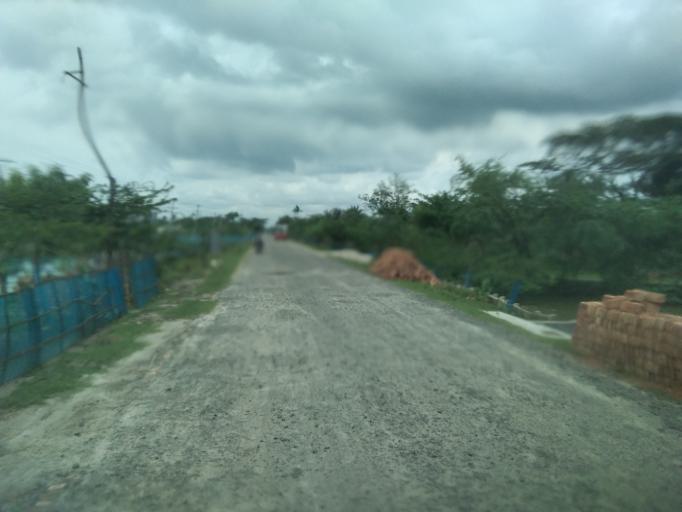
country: IN
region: West Bengal
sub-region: North 24 Parganas
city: Gosaba
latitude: 22.2665
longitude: 89.1752
